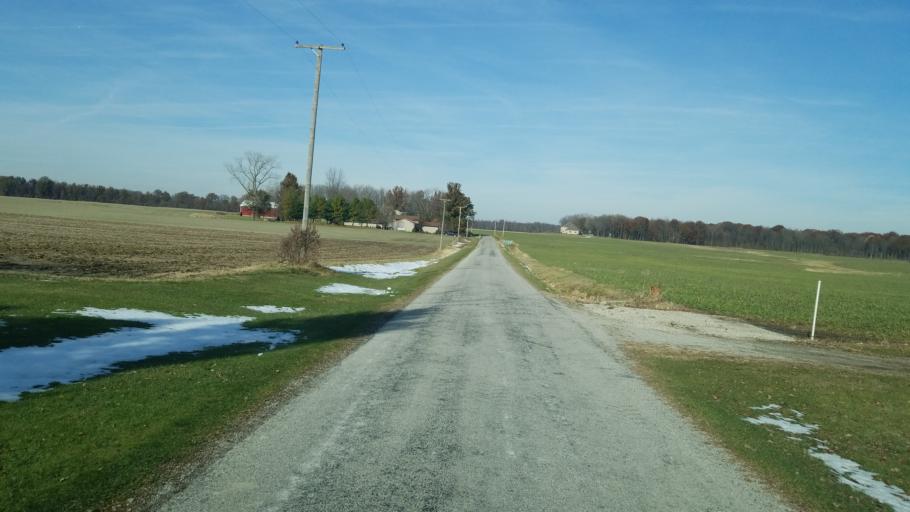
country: US
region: Ohio
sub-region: Huron County
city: Wakeman
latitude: 41.2088
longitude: -82.4112
